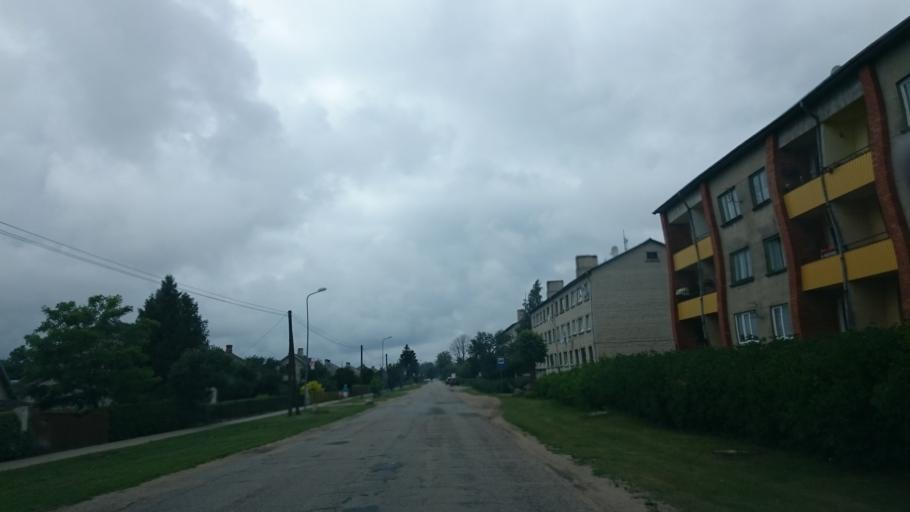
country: LV
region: Pavilostas
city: Pavilosta
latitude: 56.8837
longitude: 21.2013
